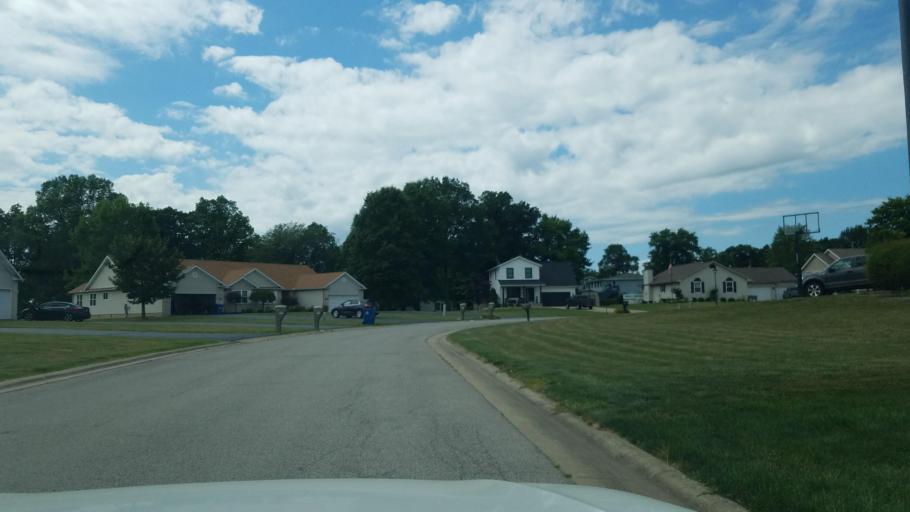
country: US
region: Ohio
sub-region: Trumbull County
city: Mineral Ridge
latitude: 41.1352
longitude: -80.7467
